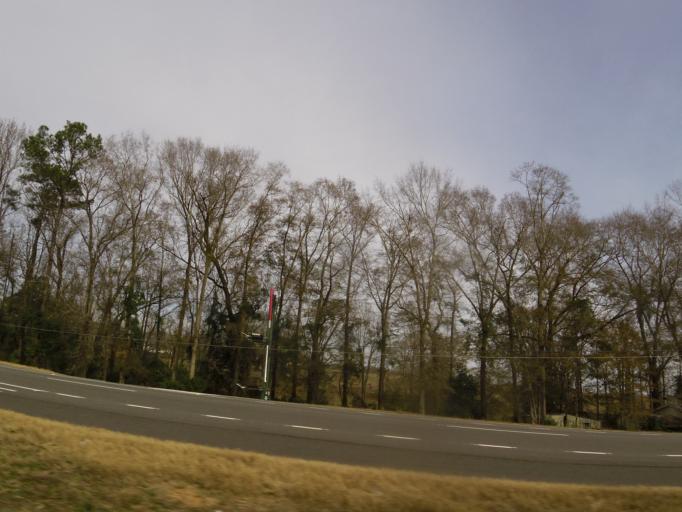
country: US
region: Alabama
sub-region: Dale County
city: Ozark
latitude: 31.5129
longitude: -85.7049
